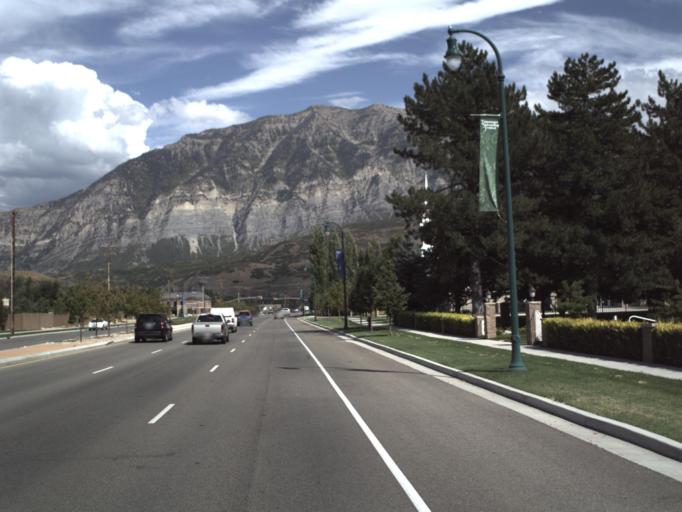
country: US
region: Utah
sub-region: Utah County
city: Orem
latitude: 40.3118
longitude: -111.6840
